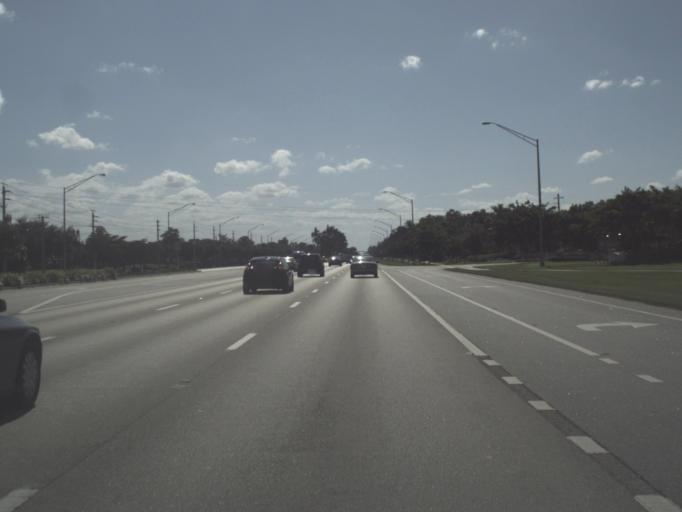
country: US
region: Florida
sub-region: Collier County
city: Lely
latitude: 26.1036
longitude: -81.7448
